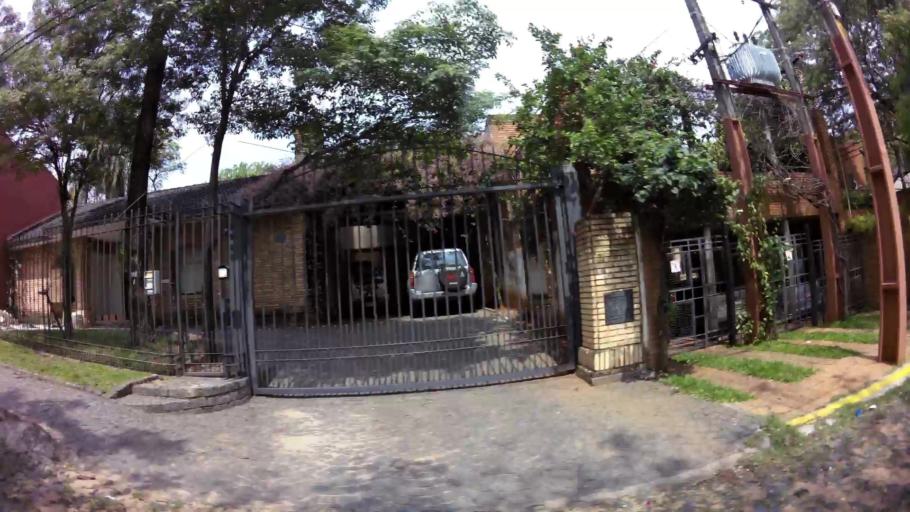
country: PY
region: Asuncion
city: Asuncion
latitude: -25.2910
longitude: -57.5812
